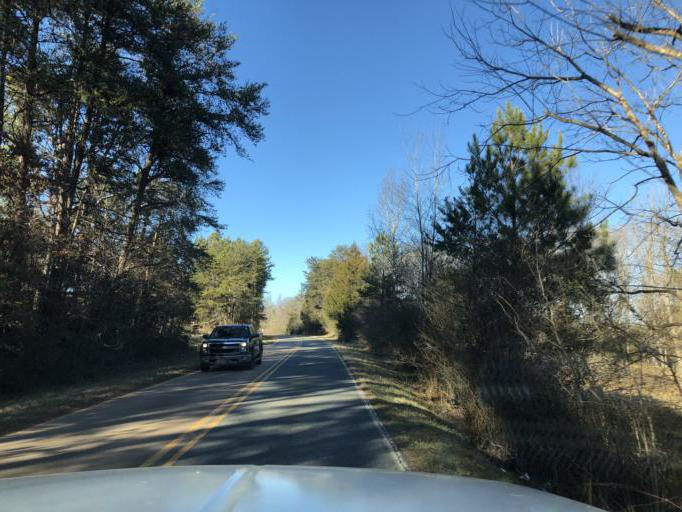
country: US
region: North Carolina
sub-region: Cleveland County
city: Shelby
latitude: 35.3334
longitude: -81.5393
